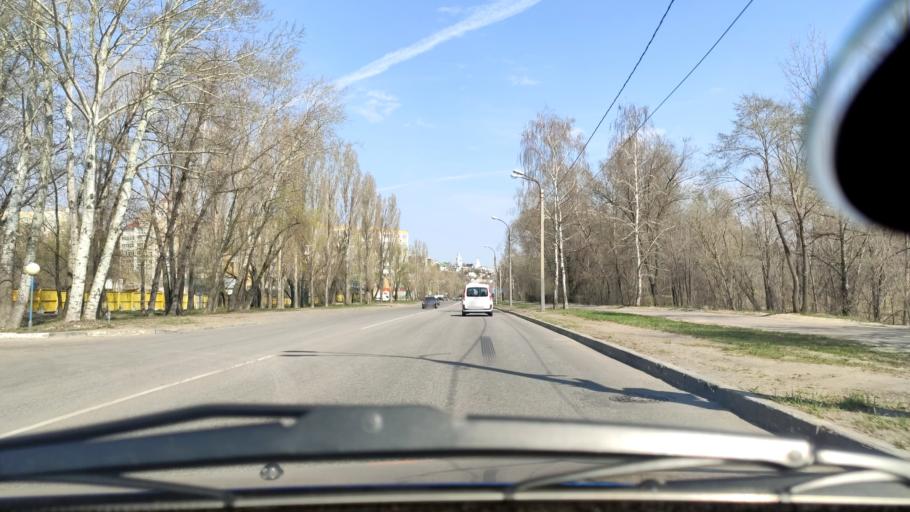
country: RU
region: Voronezj
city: Voronezh
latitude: 51.6492
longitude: 39.2116
